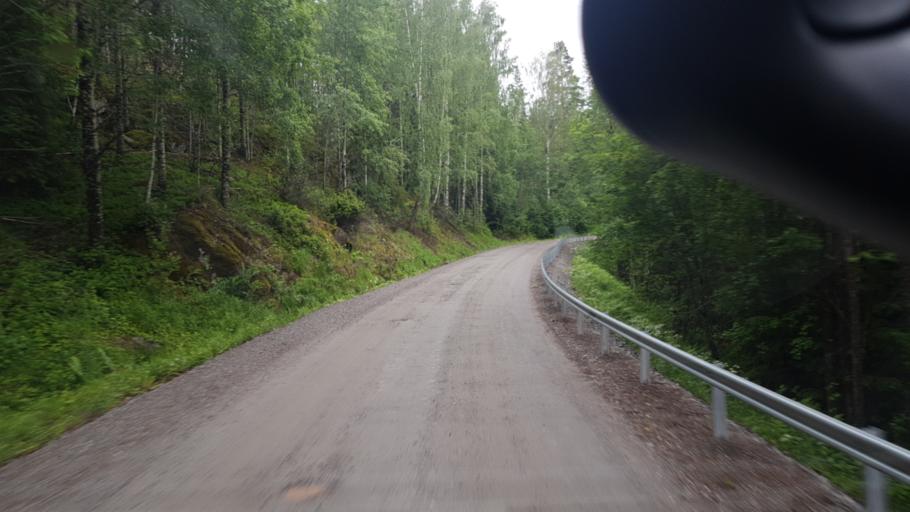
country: NO
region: Ostfold
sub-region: Romskog
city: Romskog
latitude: 59.6936
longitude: 11.9430
